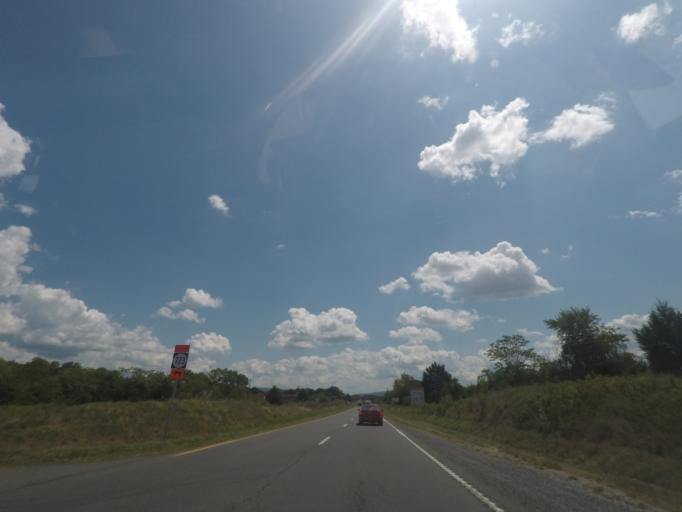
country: US
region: Virginia
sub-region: Warren County
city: Shenandoah Farms
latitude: 39.0849
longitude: -78.0875
